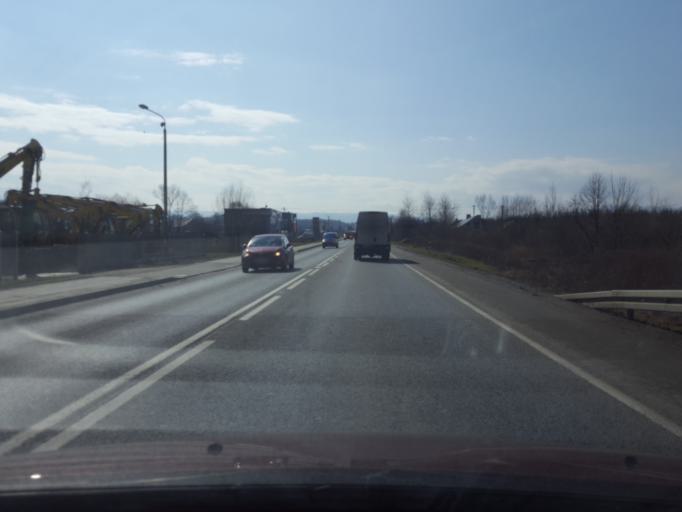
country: PL
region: Lesser Poland Voivodeship
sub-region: Powiat nowosadecki
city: Chelmiec
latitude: 49.6648
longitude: 20.6888
